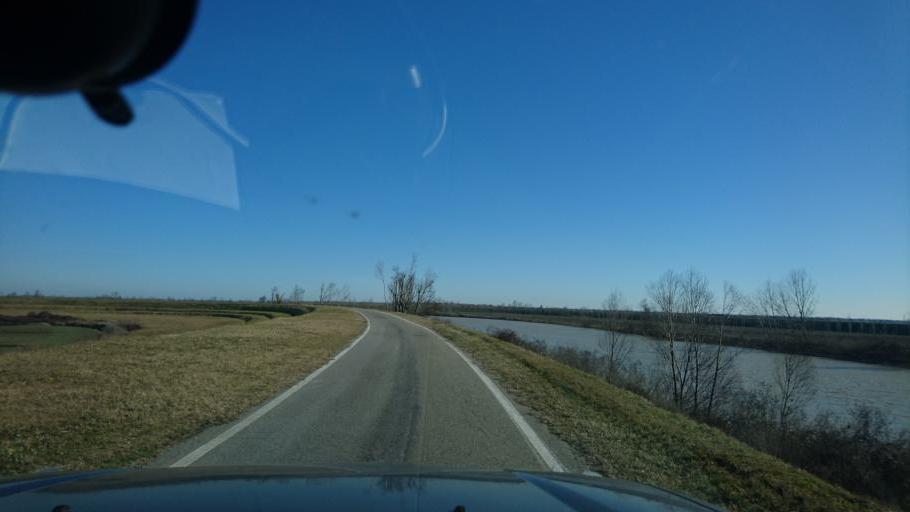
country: IT
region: Veneto
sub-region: Provincia di Rovigo
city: Ariano
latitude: 44.9316
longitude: 12.1540
